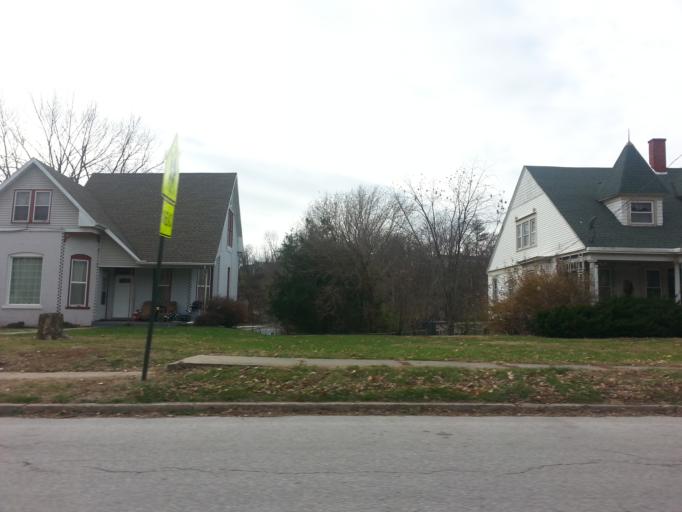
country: US
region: Missouri
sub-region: Marion County
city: Hannibal
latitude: 39.7082
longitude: -91.3880
